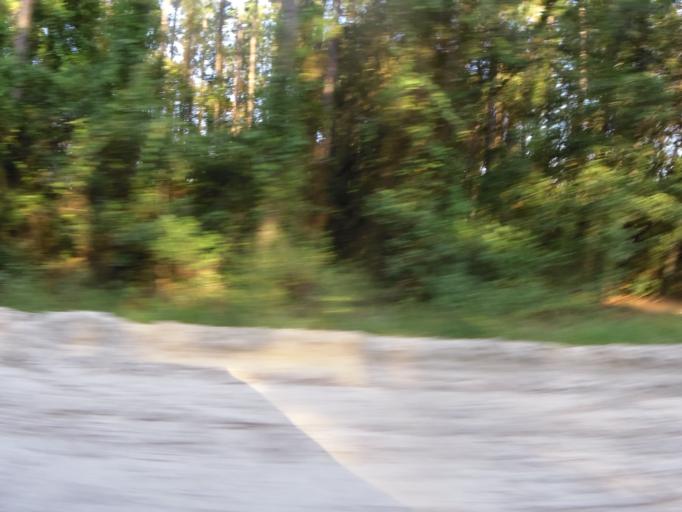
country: US
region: Florida
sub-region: Nassau County
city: Hilliard
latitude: 30.5499
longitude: -81.9950
